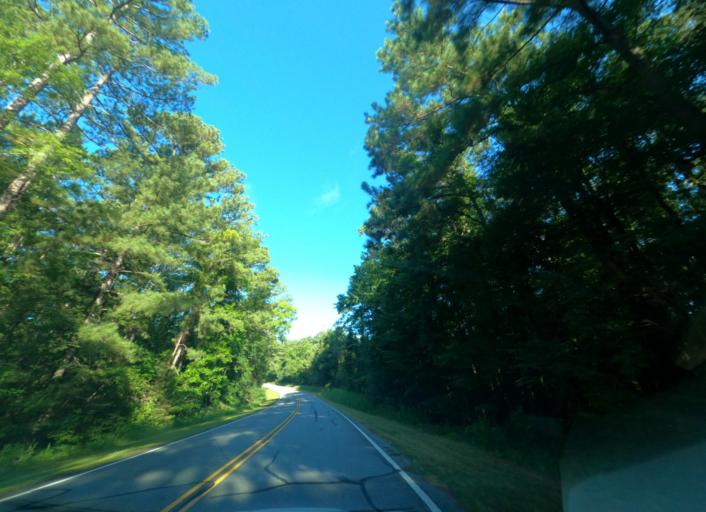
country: US
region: South Carolina
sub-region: McCormick County
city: McCormick
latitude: 33.8890
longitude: -82.4017
